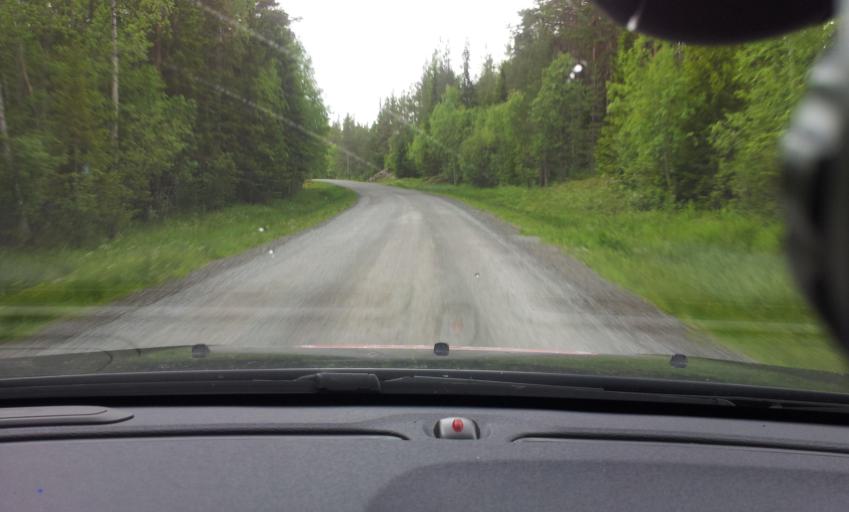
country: SE
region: Jaemtland
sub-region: OEstersunds Kommun
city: Brunflo
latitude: 63.1179
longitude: 15.0874
